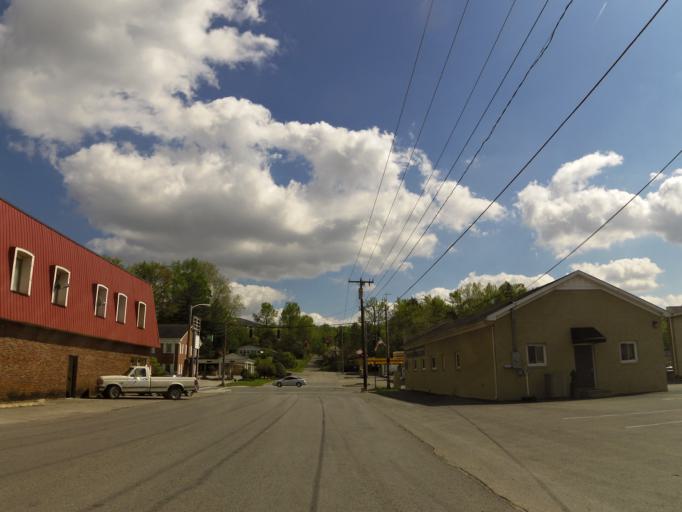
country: US
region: Kentucky
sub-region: Bell County
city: Middlesboro
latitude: 36.6084
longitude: -83.7065
